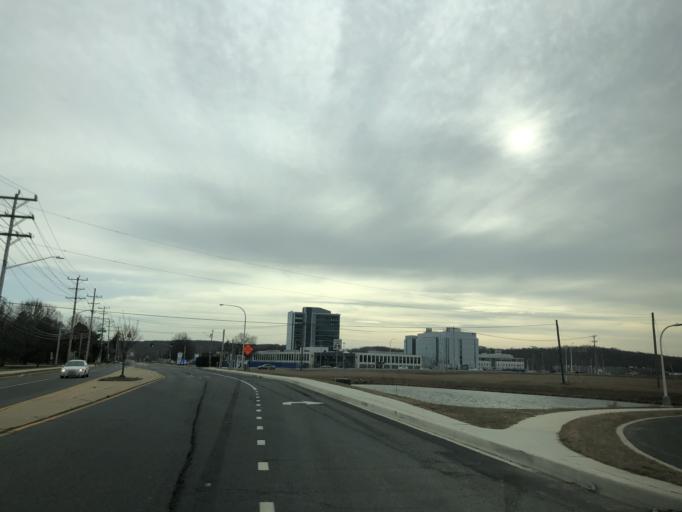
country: US
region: Delaware
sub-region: New Castle County
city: Newark
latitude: 39.6685
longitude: -75.7531
